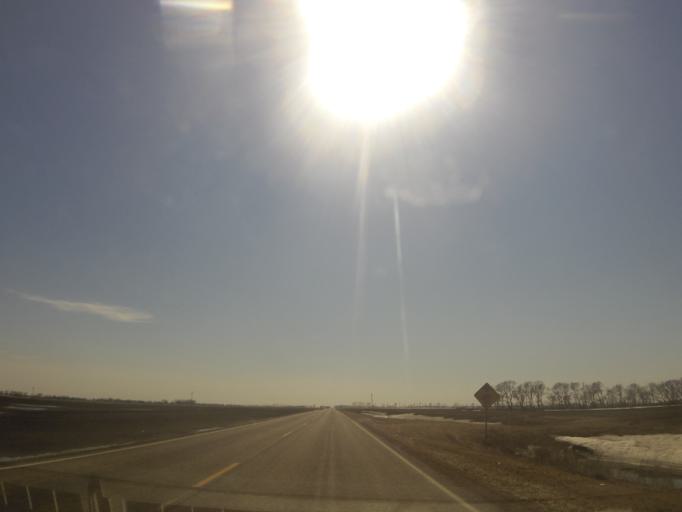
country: US
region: North Dakota
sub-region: Walsh County
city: Grafton
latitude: 48.4165
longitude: -97.2996
